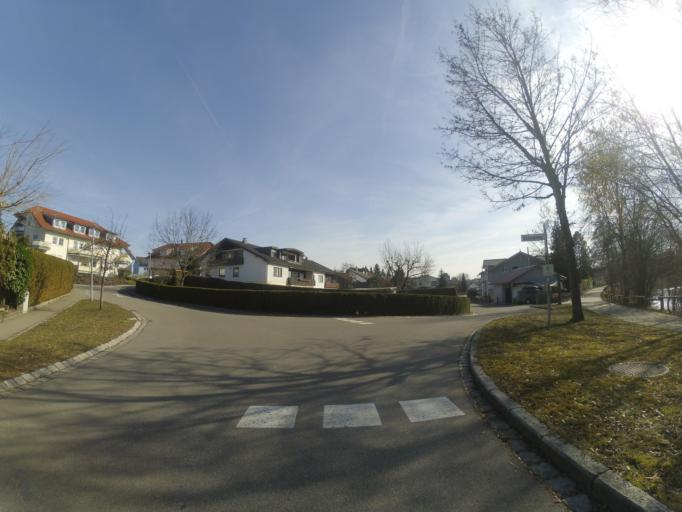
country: DE
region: Baden-Wuerttemberg
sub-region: Tuebingen Region
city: Meckenbeuren
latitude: 47.6843
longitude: 9.5519
